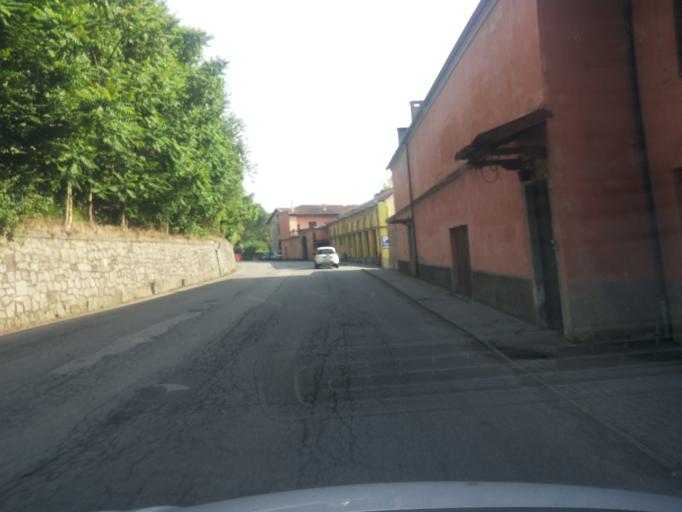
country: IT
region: Piedmont
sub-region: Provincia di Biella
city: Andorno Cacciorna
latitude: 45.6012
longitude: 8.0567
